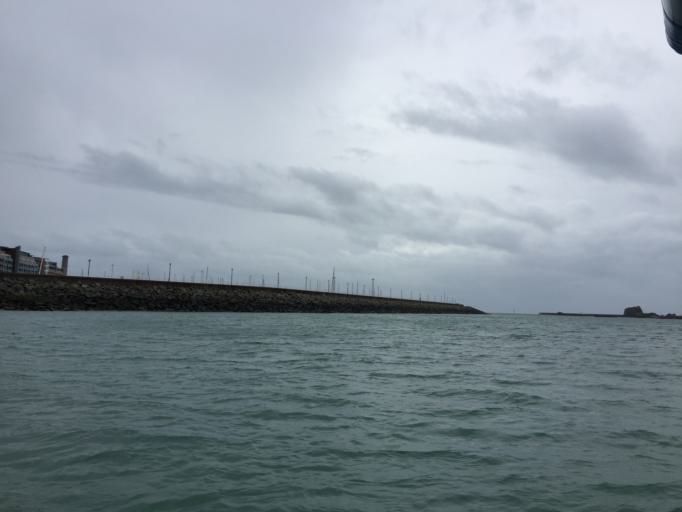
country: JE
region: St Helier
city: Saint Helier
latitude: 49.1849
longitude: -2.1188
